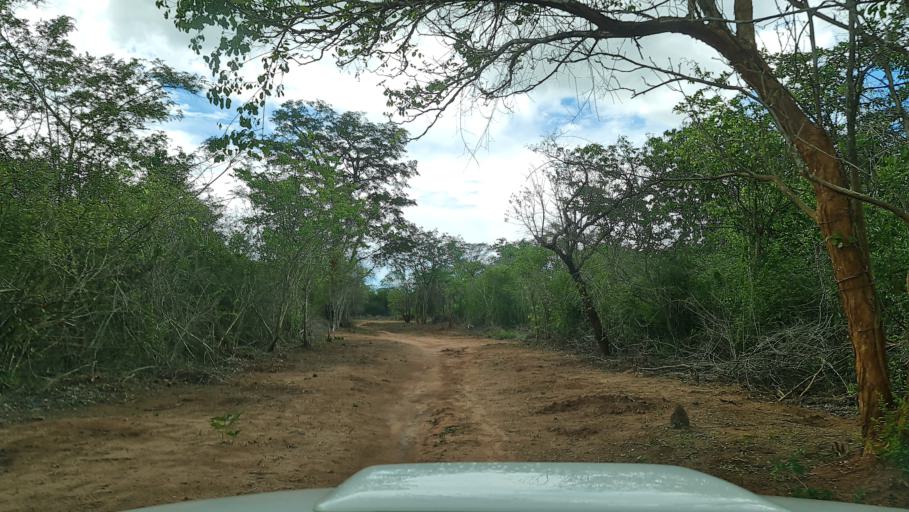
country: MZ
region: Nampula
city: Ilha de Mocambique
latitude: -15.5008
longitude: 40.1800
